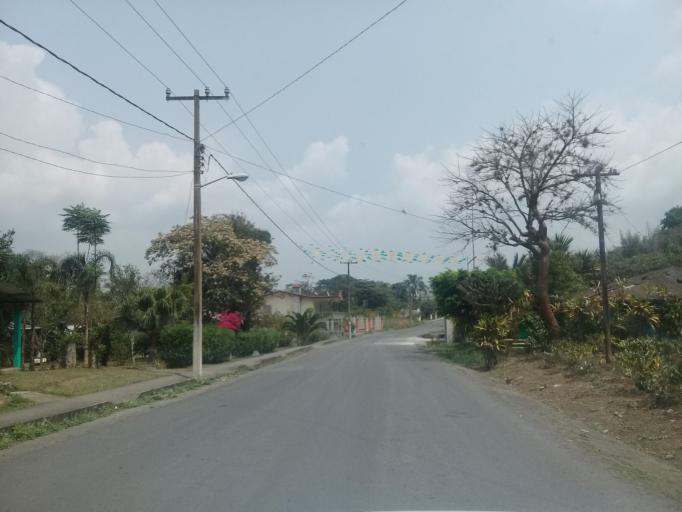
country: MX
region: Veracruz
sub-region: Ixtaczoquitlan
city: Capoluca
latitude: 18.8124
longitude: -96.9848
